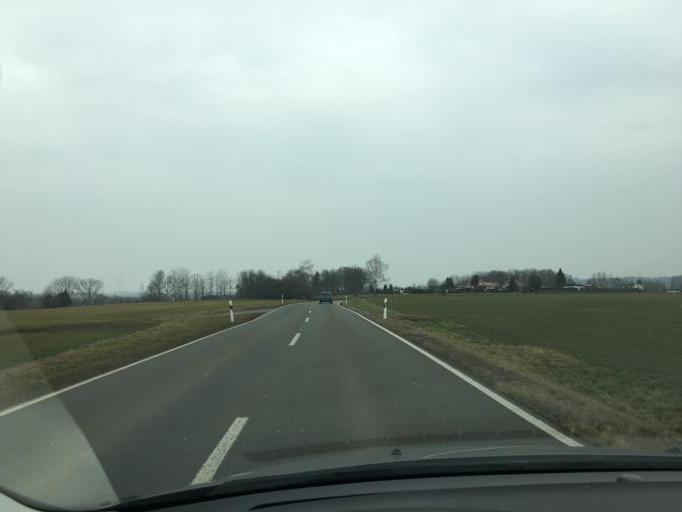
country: DE
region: Thuringia
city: Gerstenberg
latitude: 51.0275
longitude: 12.4473
